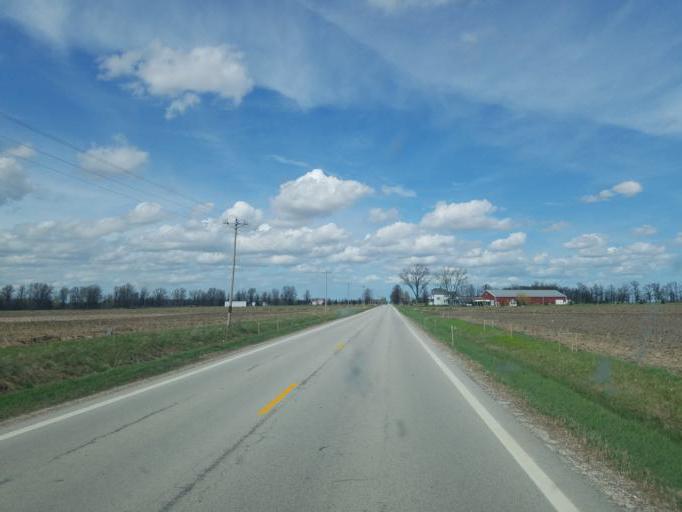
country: US
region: Ohio
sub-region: Huron County
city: Bellevue
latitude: 41.2089
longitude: -82.8205
